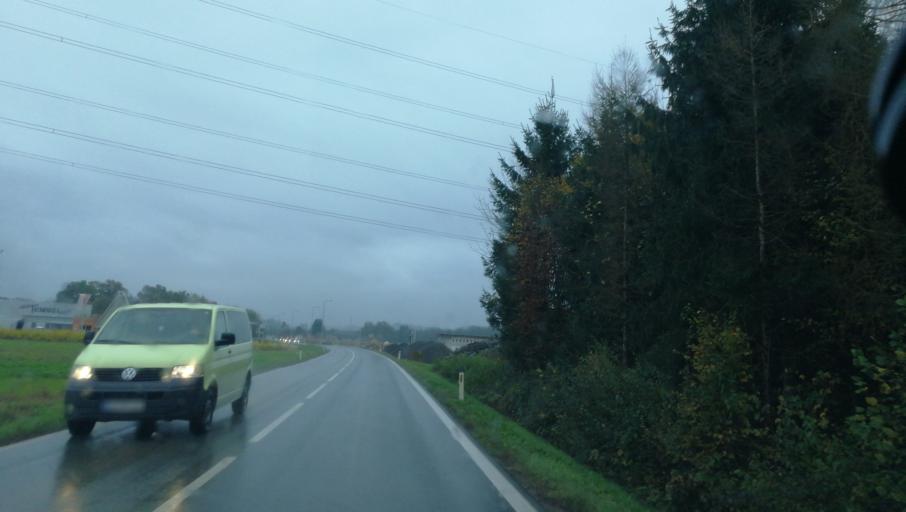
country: AT
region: Styria
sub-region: Politischer Bezirk Leibnitz
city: Spielfeld
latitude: 46.7204
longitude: 15.6531
